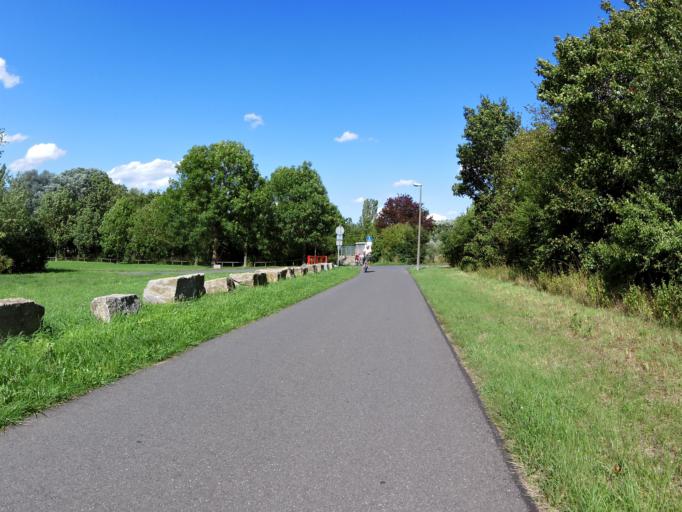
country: DE
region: Bavaria
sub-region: Regierungsbezirk Unterfranken
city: Kitzingen
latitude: 49.7283
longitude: 10.1680
